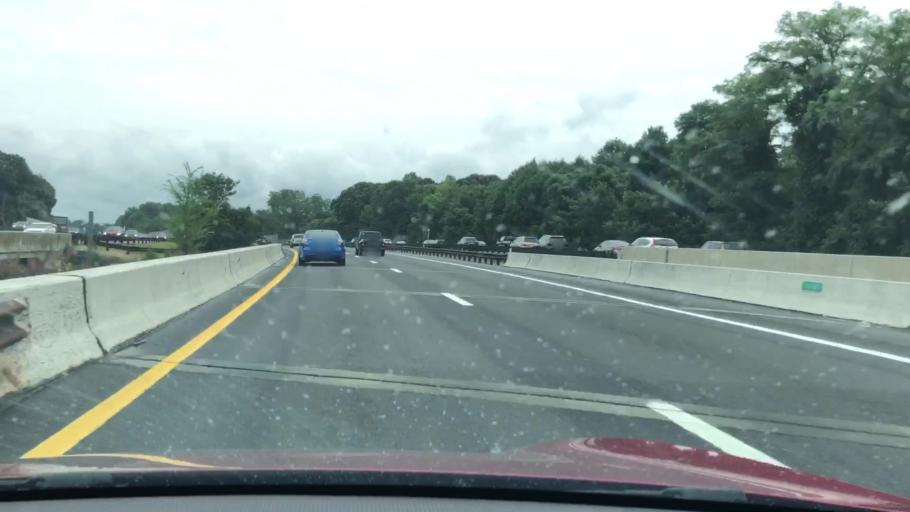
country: US
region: New Jersey
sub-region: Monmouth County
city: Lincroft
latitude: 40.3450
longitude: -74.1143
